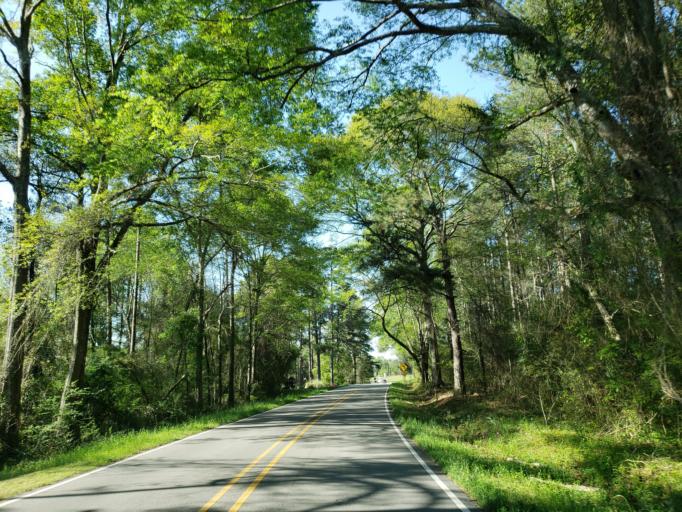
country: US
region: Mississippi
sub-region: Covington County
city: Collins
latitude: 31.6093
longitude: -89.3818
